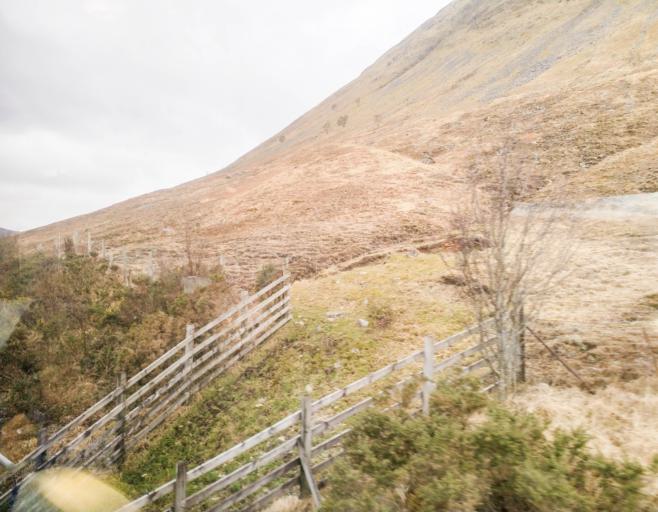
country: GB
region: Scotland
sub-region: Argyll and Bute
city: Garelochhead
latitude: 56.4878
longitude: -4.7223
